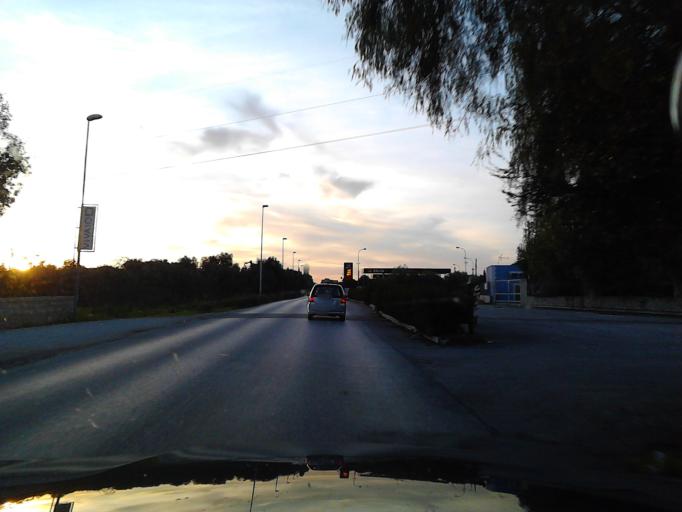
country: IT
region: Apulia
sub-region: Provincia di Bari
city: Valenzano
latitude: 41.0461
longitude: 16.9026
